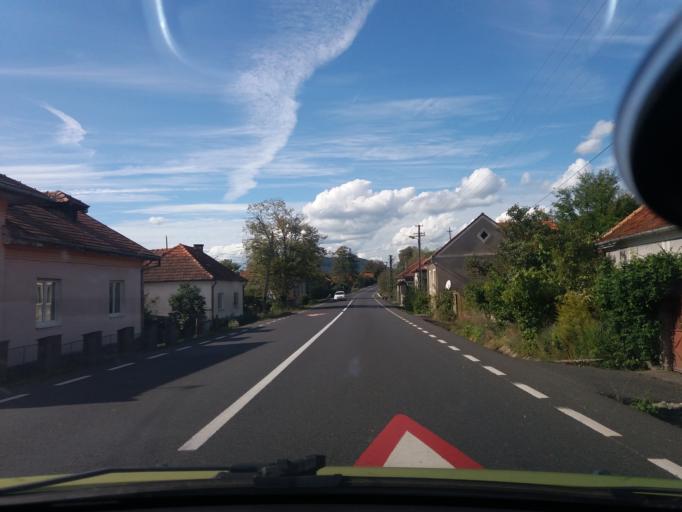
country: RO
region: Hunedoara
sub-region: Comuna Burjuc
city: Burjuc
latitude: 45.9496
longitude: 22.4899
